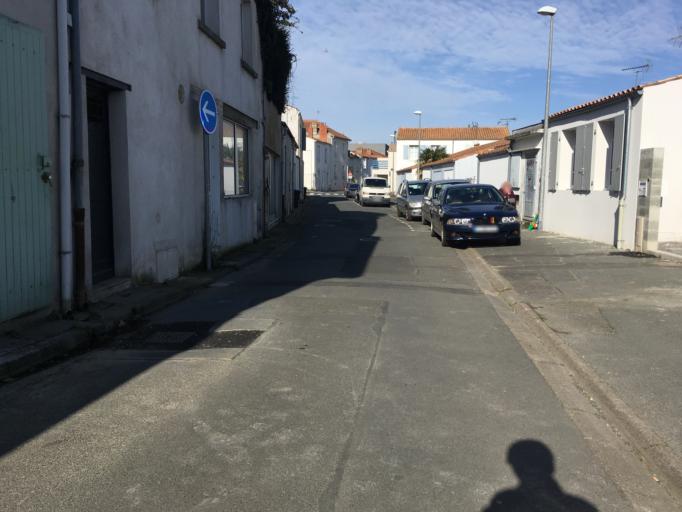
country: FR
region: Poitou-Charentes
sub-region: Departement de la Charente-Maritime
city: La Rochelle
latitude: 46.1490
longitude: -1.1437
